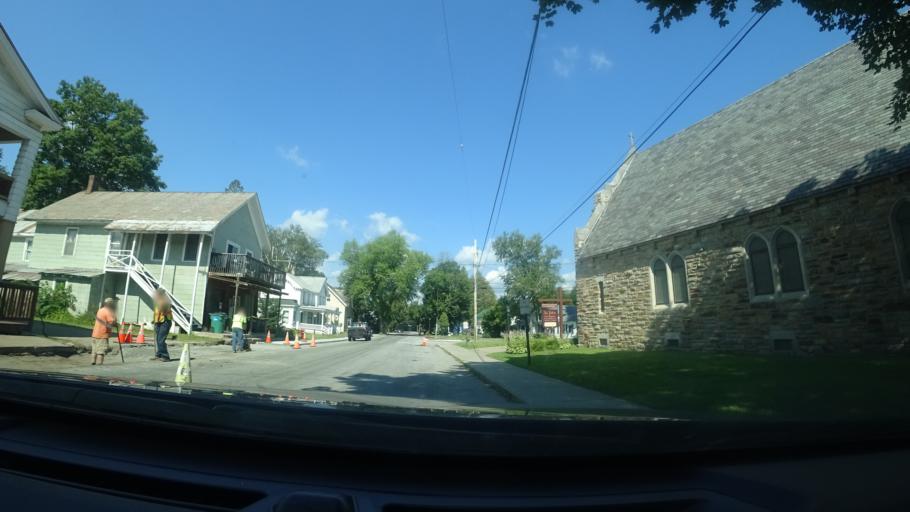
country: US
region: New York
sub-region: Warren County
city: Warrensburg
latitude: 43.6534
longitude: -73.8027
